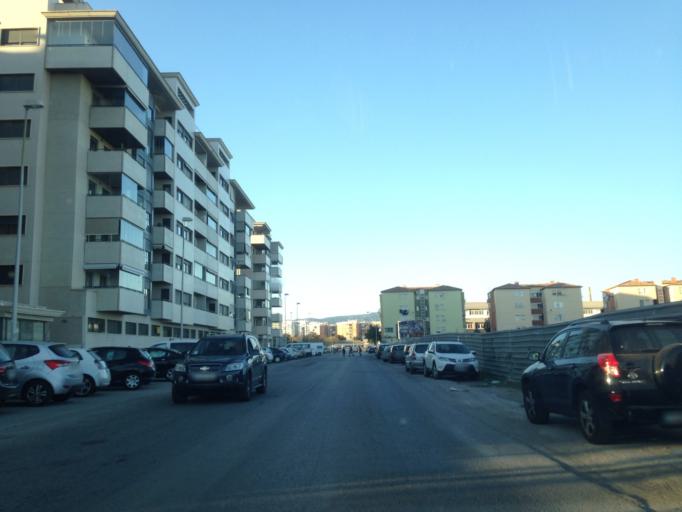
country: ES
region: Andalusia
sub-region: Provincia de Malaga
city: Malaga
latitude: 36.6855
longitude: -4.4485
